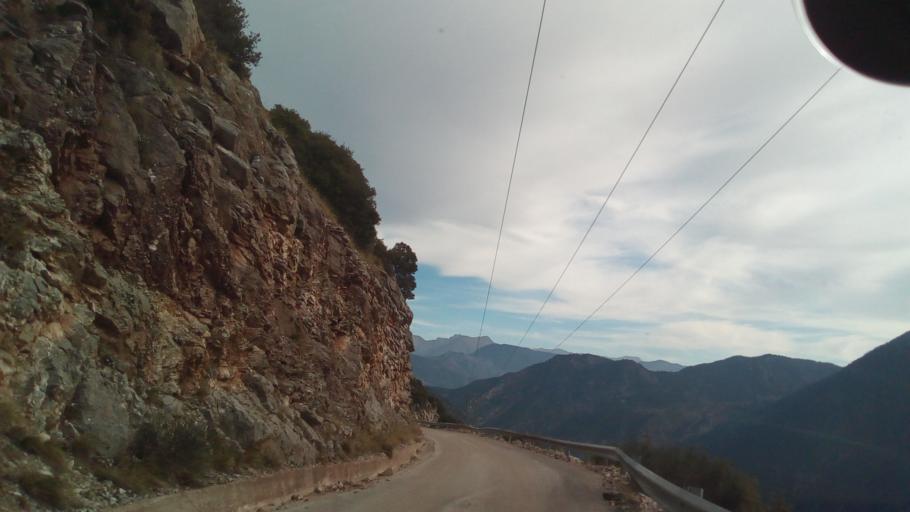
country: GR
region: West Greece
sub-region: Nomos Aitolias kai Akarnanias
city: Thermo
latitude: 38.6746
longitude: 21.8882
